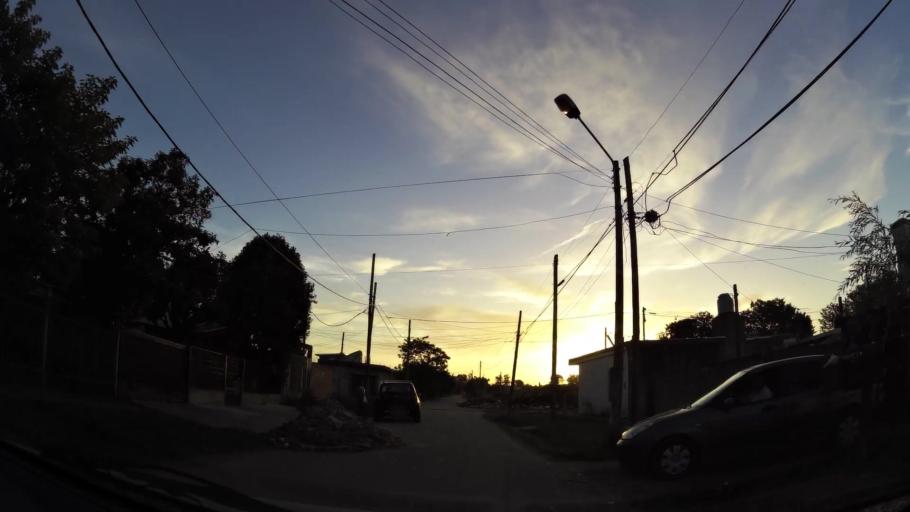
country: AR
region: Buenos Aires
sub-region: Partido de Quilmes
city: Quilmes
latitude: -34.7840
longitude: -58.2277
